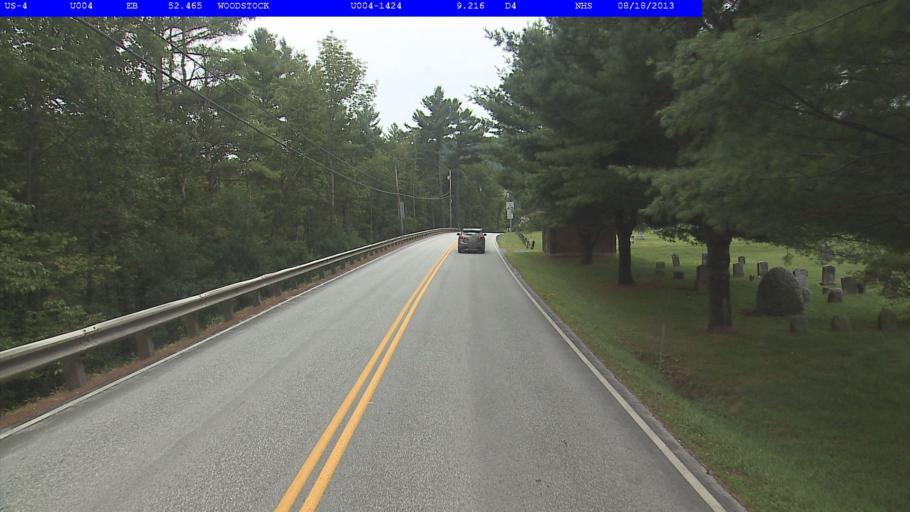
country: US
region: Vermont
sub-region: Windsor County
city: Woodstock
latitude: 43.6357
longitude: -72.4712
